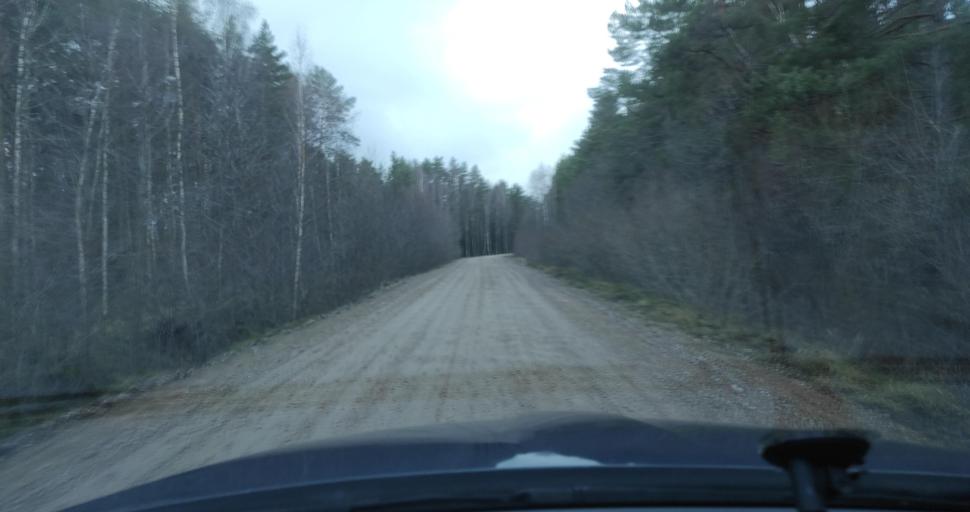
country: LV
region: Pavilostas
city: Pavilosta
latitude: 56.8477
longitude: 21.1035
